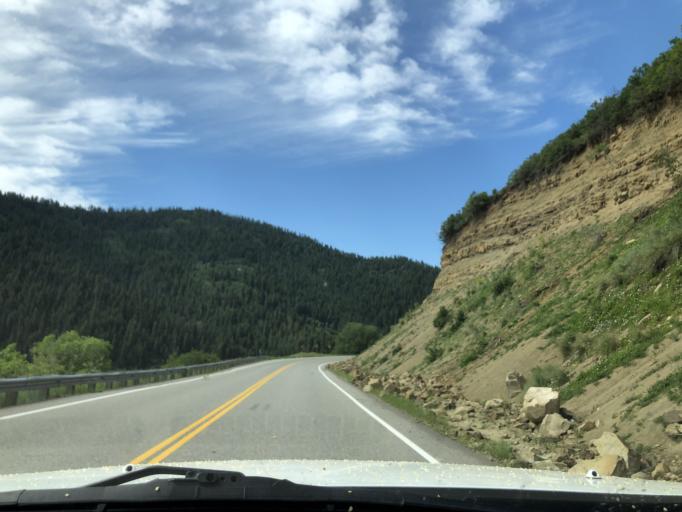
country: US
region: Colorado
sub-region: Delta County
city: Paonia
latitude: 38.9508
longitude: -107.3452
